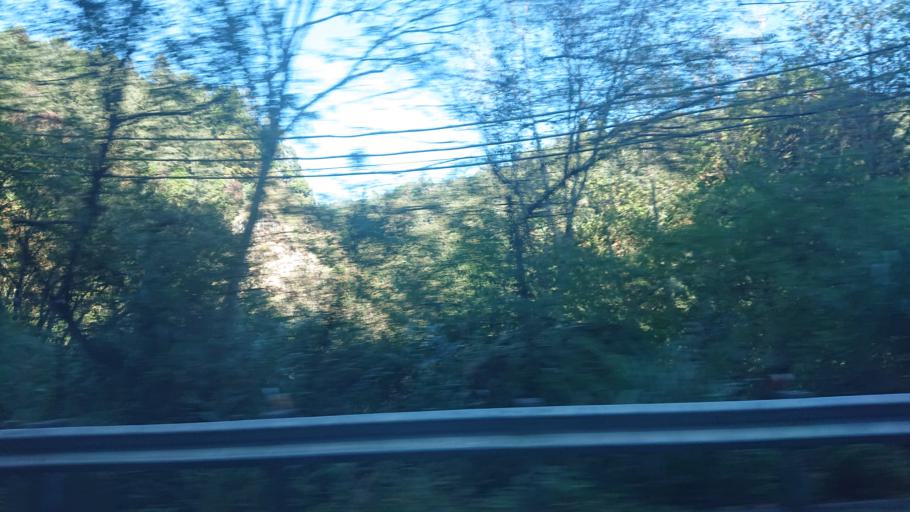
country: TW
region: Taiwan
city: Lugu
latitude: 23.5057
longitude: 120.8163
